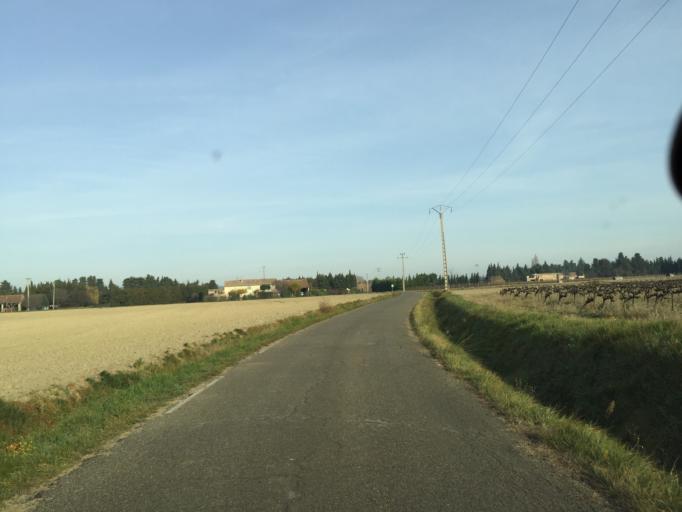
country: FR
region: Provence-Alpes-Cote d'Azur
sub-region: Departement du Vaucluse
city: Serignan-du-Comtat
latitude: 44.1647
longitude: 4.8388
